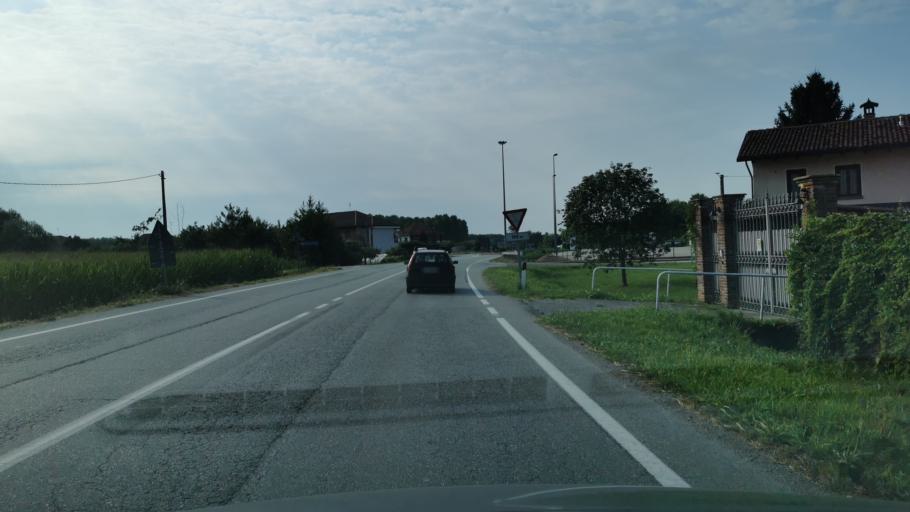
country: IT
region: Piedmont
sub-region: Provincia di Torino
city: Cercenasco
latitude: 44.8628
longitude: 7.5085
